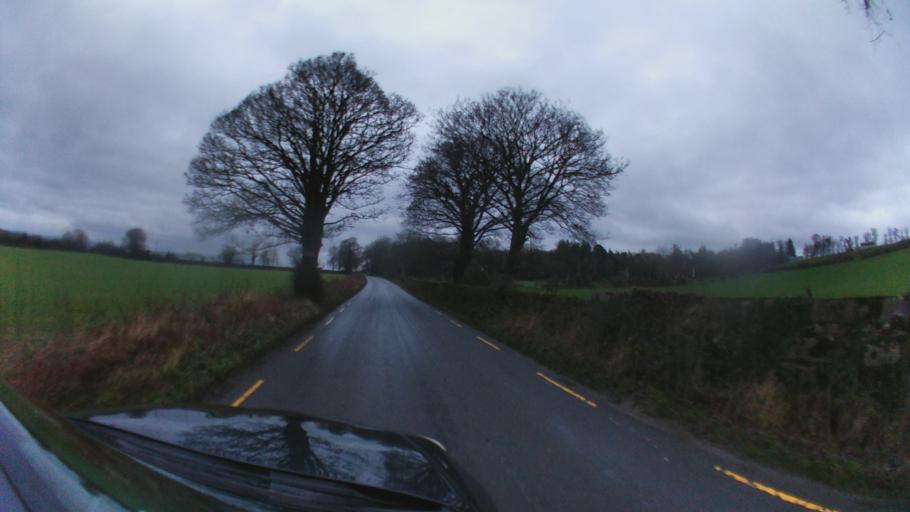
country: IE
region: Leinster
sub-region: Kilkenny
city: Graiguenamanagh
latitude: 52.6025
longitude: -6.9919
